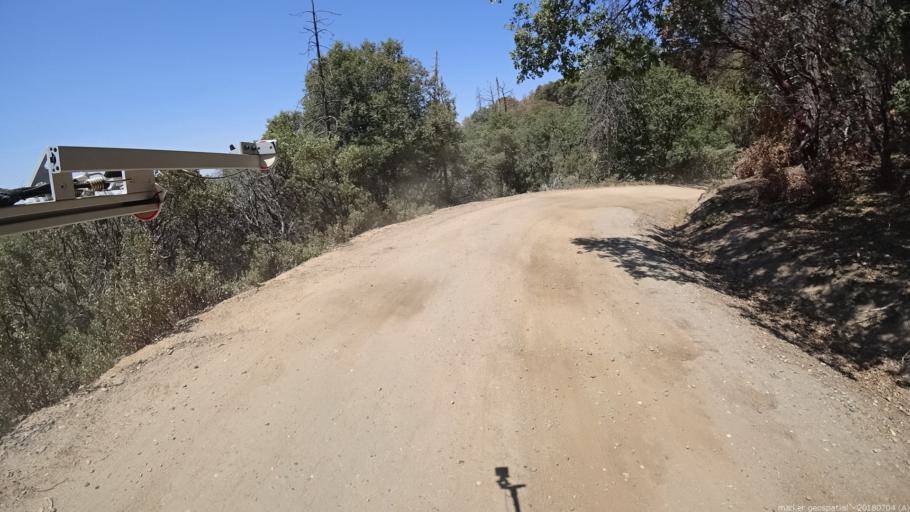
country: US
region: California
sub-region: Fresno County
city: Auberry
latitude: 37.2364
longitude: -119.4575
